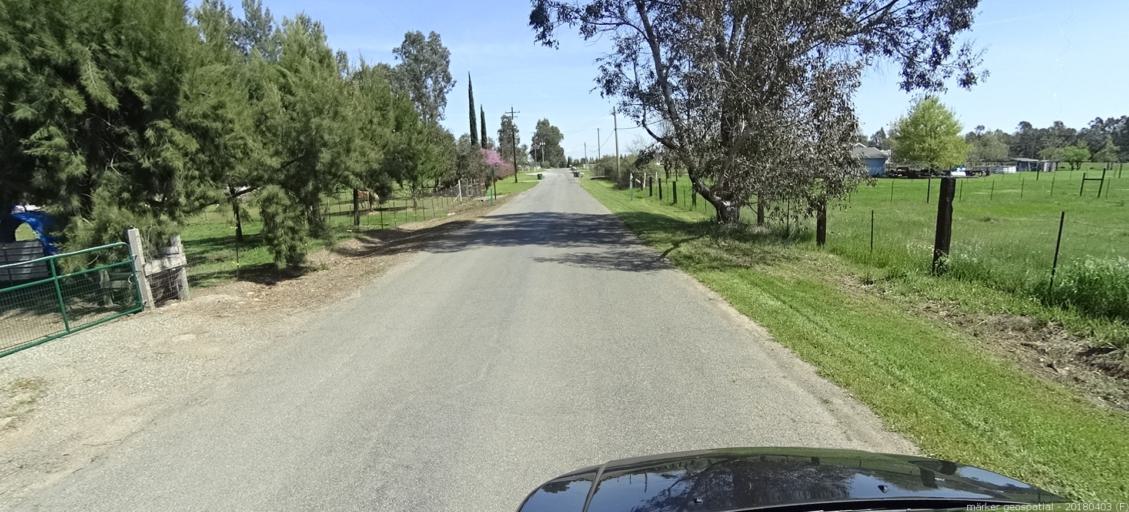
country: US
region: California
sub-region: Sacramento County
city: Clay
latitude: 38.3577
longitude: -121.2072
